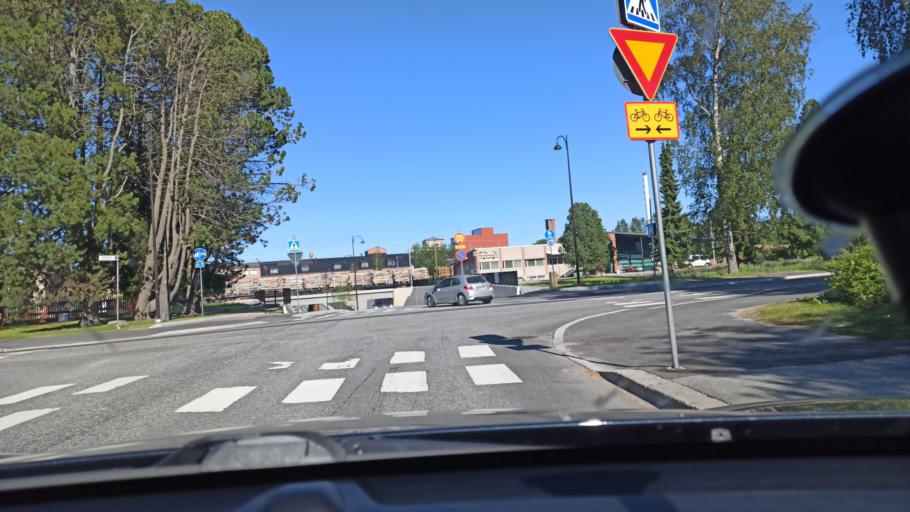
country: FI
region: Ostrobothnia
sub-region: Jakobstadsregionen
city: Jakobstad
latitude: 63.6747
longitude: 22.7117
